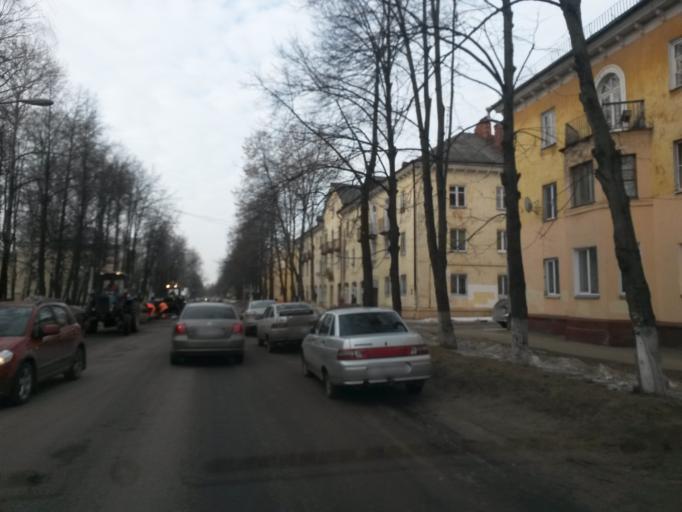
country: RU
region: Jaroslavl
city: Yaroslavl
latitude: 57.6352
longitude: 39.8464
